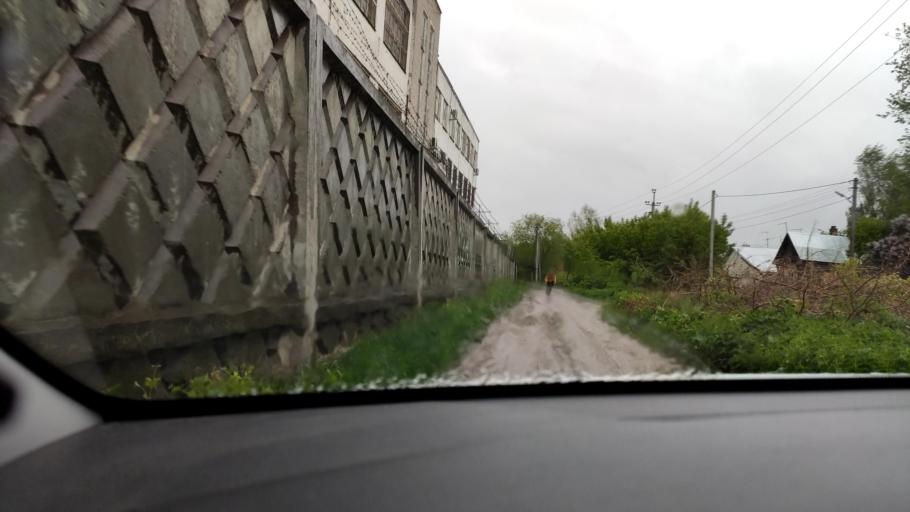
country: RU
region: Tatarstan
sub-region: Gorod Kazan'
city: Kazan
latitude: 55.7534
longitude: 49.1354
